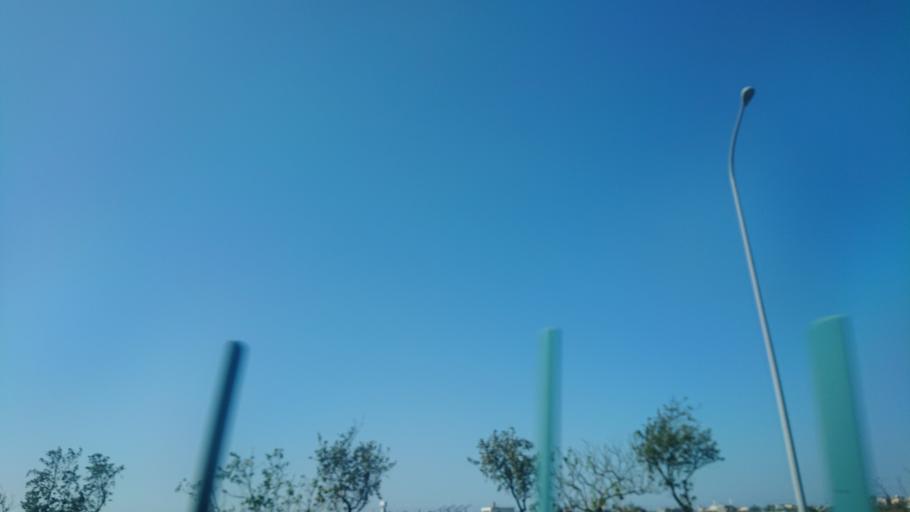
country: TW
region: Taiwan
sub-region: Chiayi
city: Taibao
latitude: 23.6088
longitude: 120.1651
